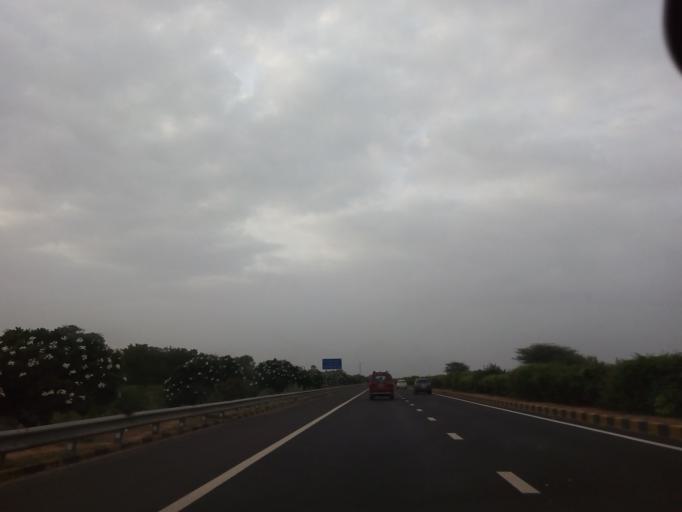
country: IN
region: Gujarat
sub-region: Kheda
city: Mahemdavad
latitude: 22.9027
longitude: 72.7736
